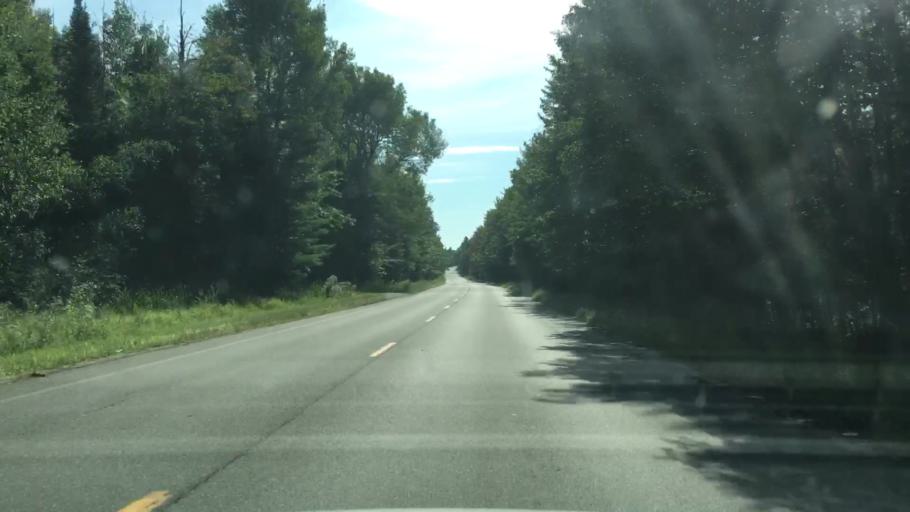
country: US
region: Maine
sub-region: Penobscot County
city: Lincoln
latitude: 45.3885
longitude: -68.5359
